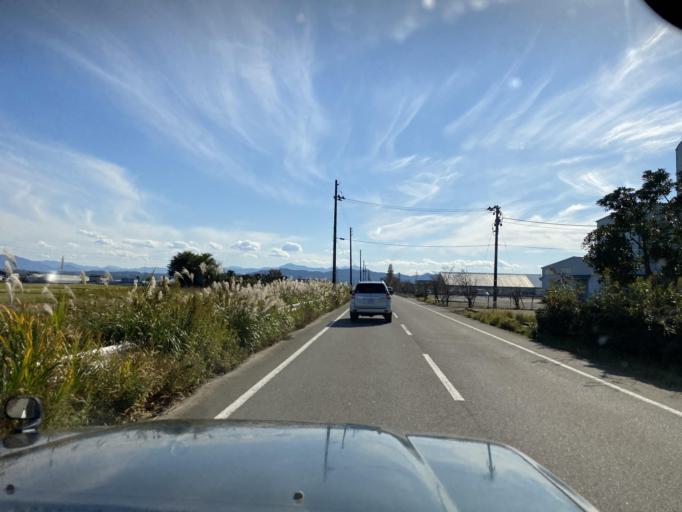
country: JP
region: Niigata
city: Niitsu-honcho
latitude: 37.7955
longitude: 139.0783
